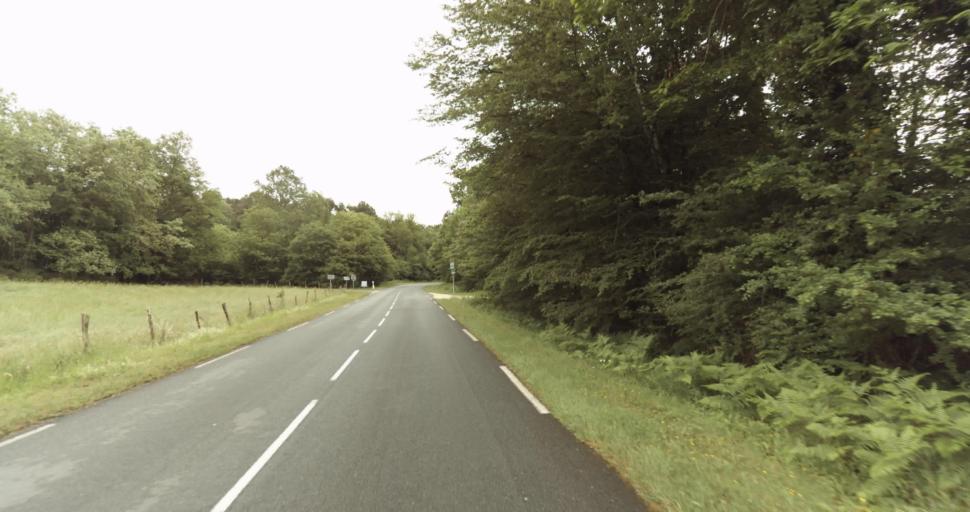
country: FR
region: Aquitaine
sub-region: Departement de la Dordogne
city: Belves
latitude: 44.6778
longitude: 0.9929
